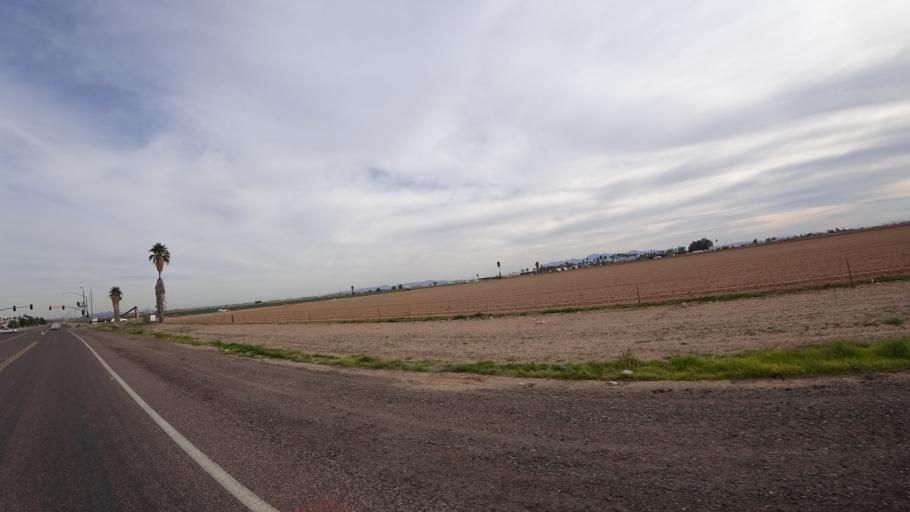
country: US
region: Arizona
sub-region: Maricopa County
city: El Mirage
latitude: 33.5802
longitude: -112.3606
